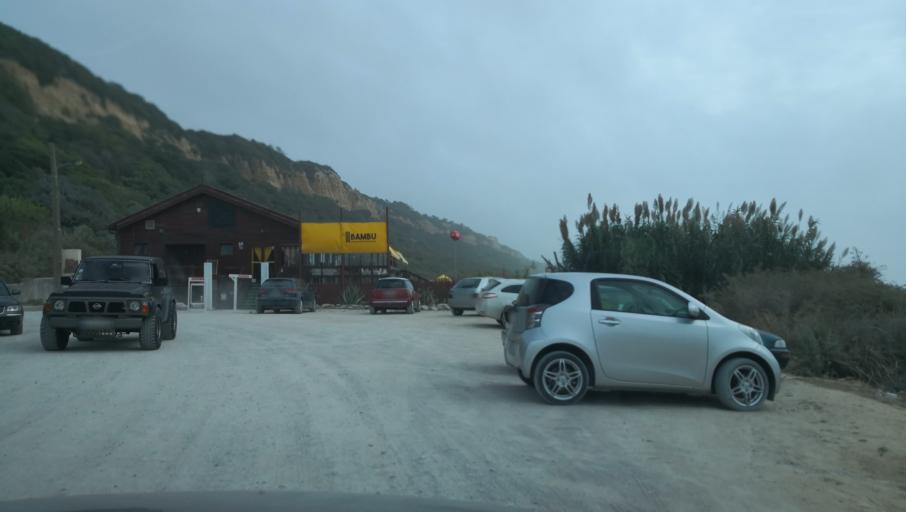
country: PT
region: Setubal
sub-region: Almada
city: Charneca
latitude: 38.5656
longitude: -9.1924
